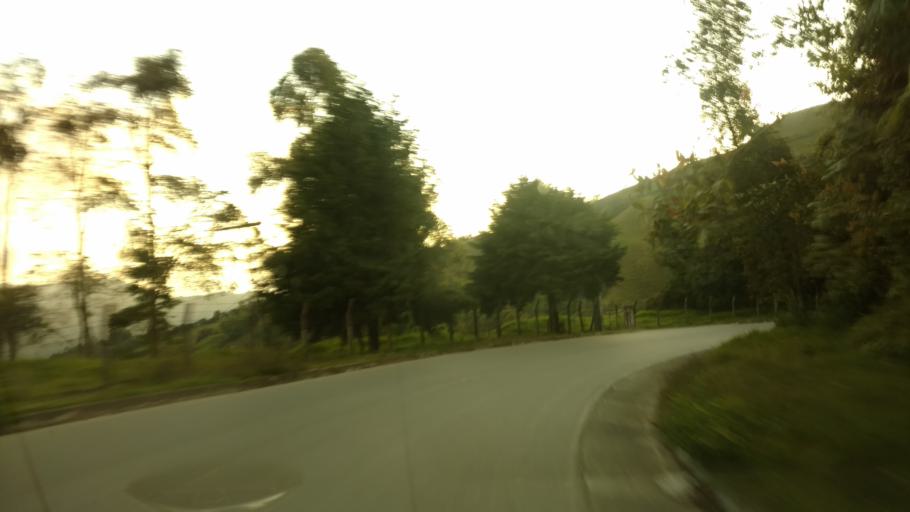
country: CO
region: Caldas
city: Aranzazu
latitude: 5.2825
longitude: -75.4880
